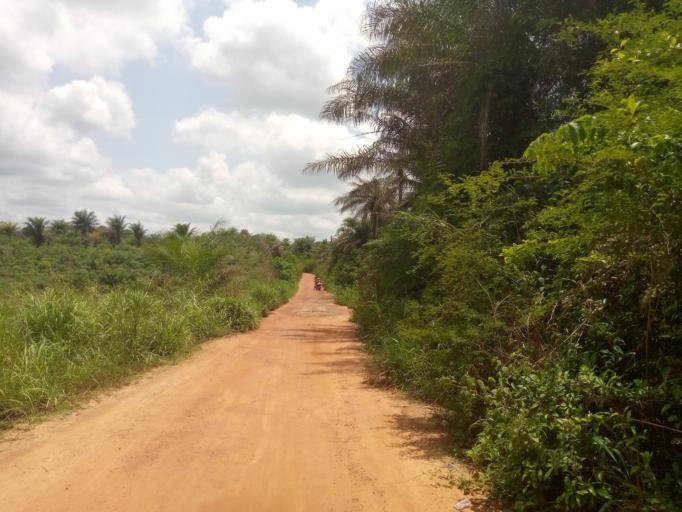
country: SL
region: Western Area
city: Waterloo
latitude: 8.3755
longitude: -12.9648
